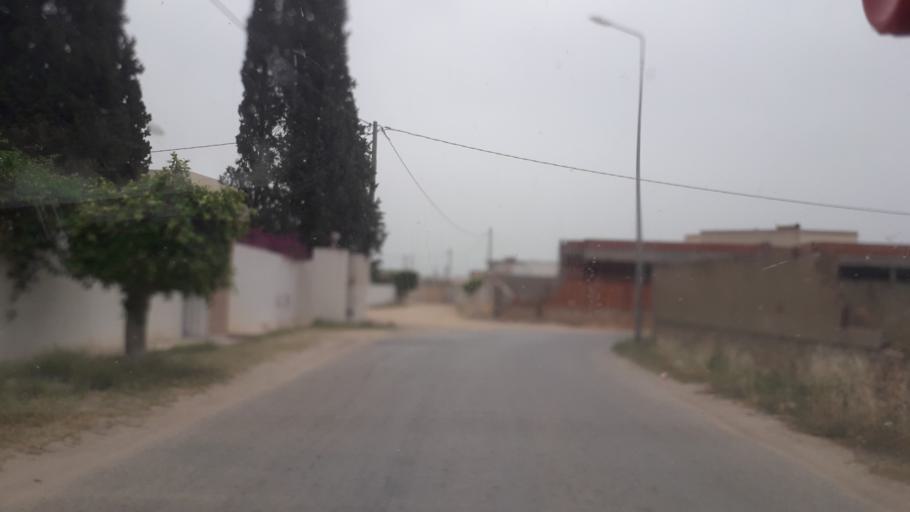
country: TN
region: Safaqis
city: Al Qarmadah
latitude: 34.7909
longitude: 10.7623
